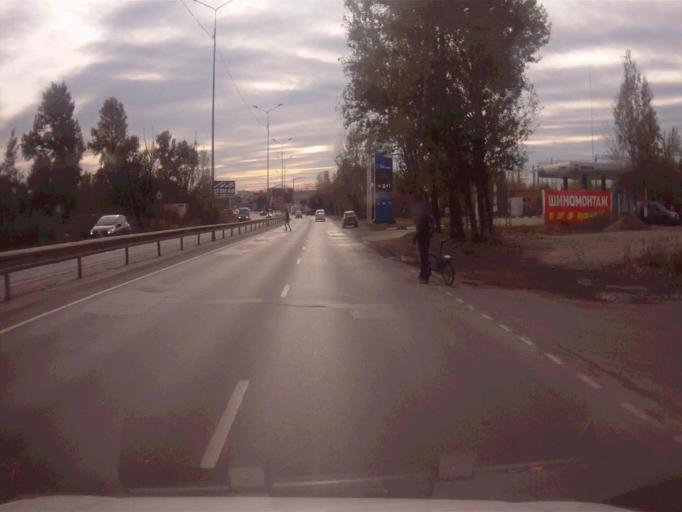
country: RU
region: Chelyabinsk
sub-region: Gorod Chelyabinsk
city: Chelyabinsk
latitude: 55.1137
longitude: 61.4127
